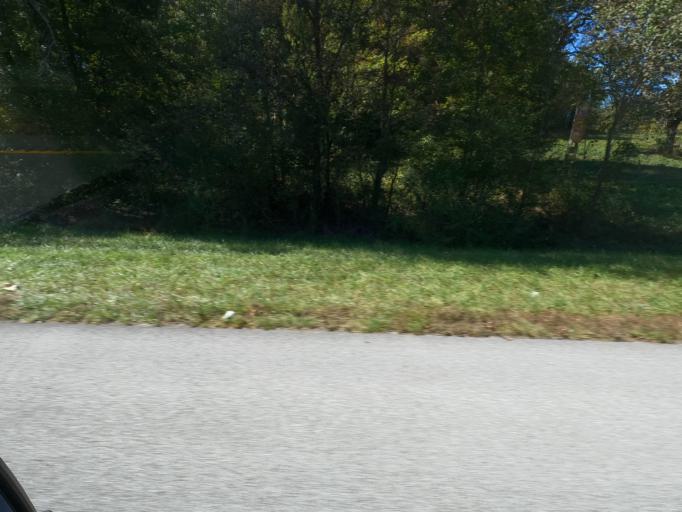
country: US
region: Tennessee
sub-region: Maury County
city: Mount Pleasant
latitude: 35.4133
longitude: -87.2820
